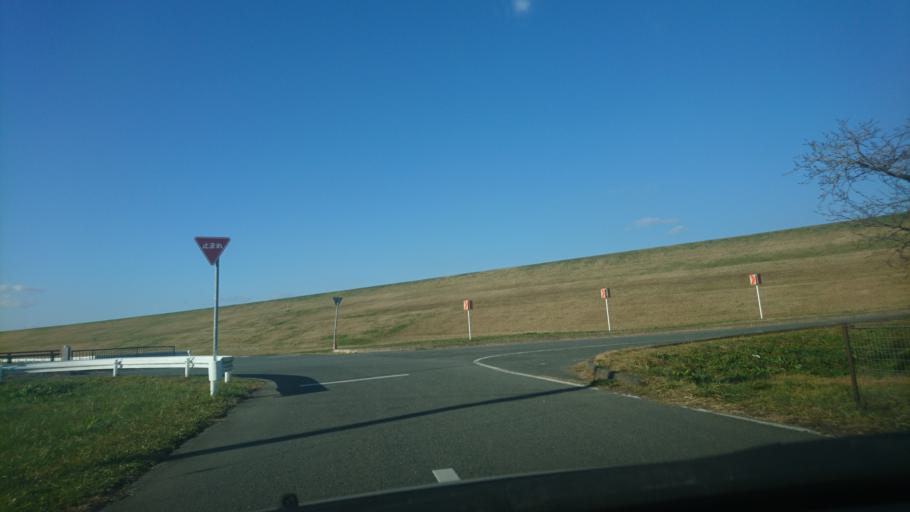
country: JP
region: Iwate
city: Ichinoseki
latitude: 38.9418
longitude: 141.1562
